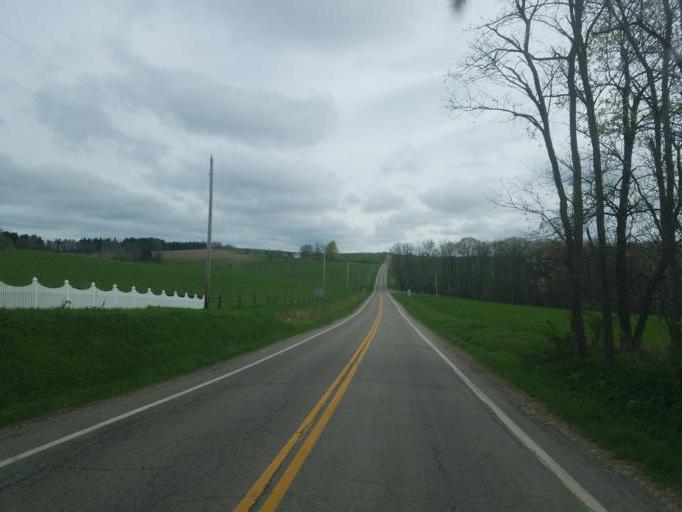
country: US
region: Ohio
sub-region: Ashland County
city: Loudonville
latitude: 40.5513
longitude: -82.1679
